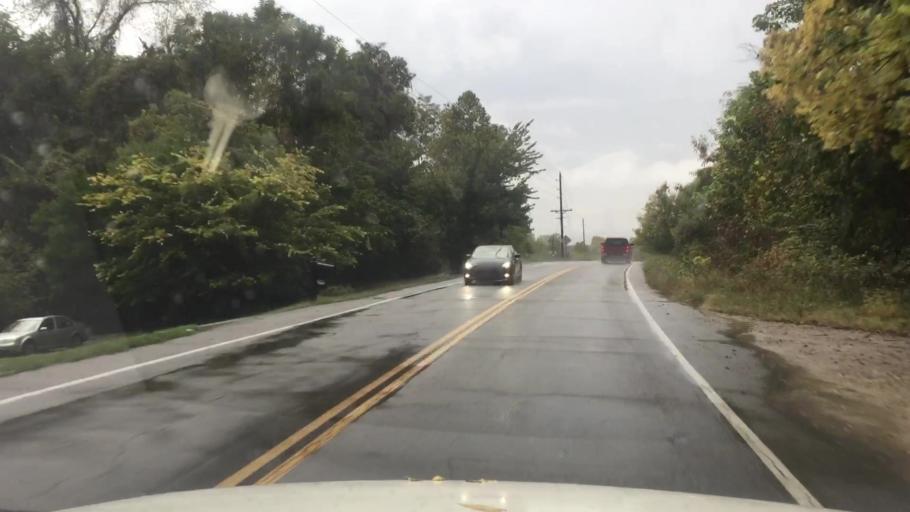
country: US
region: Missouri
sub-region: Boone County
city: Columbia
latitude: 38.8857
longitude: -92.4368
